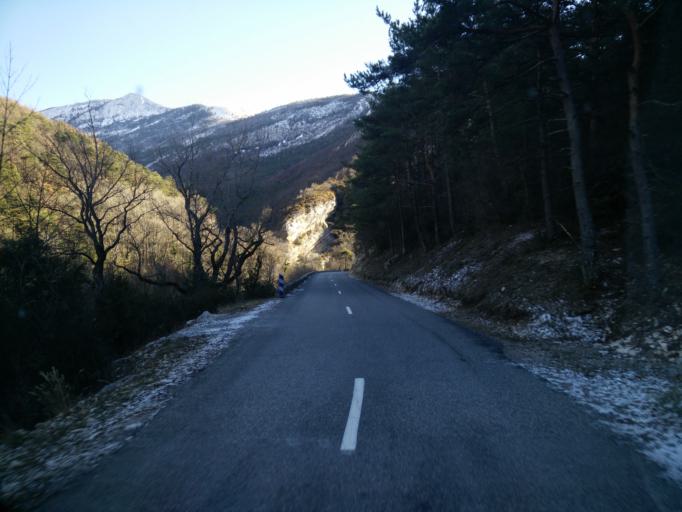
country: FR
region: Provence-Alpes-Cote d'Azur
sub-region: Departement des Alpes-de-Haute-Provence
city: Castellane
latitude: 43.8195
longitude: 6.4340
